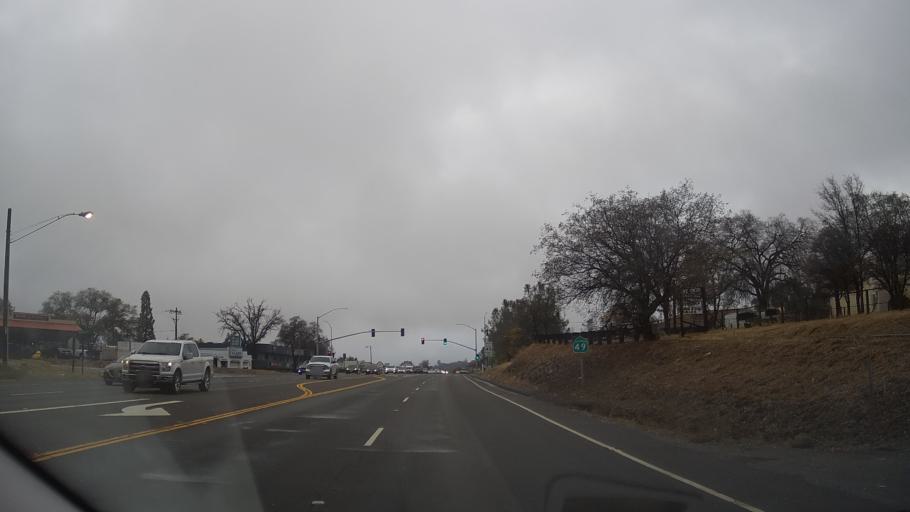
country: US
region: California
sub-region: Placer County
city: North Auburn
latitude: 38.9192
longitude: -121.0813
